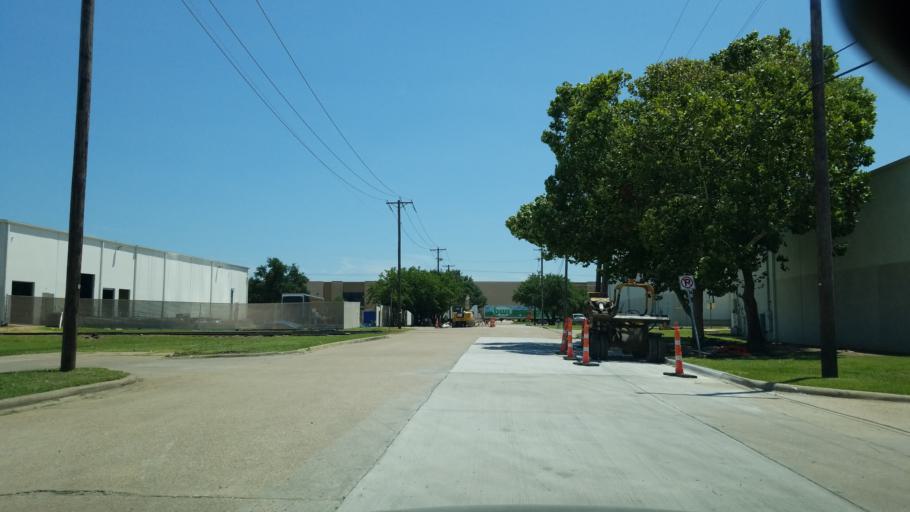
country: US
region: Texas
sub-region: Dallas County
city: Carrollton
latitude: 32.9479
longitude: -96.9141
